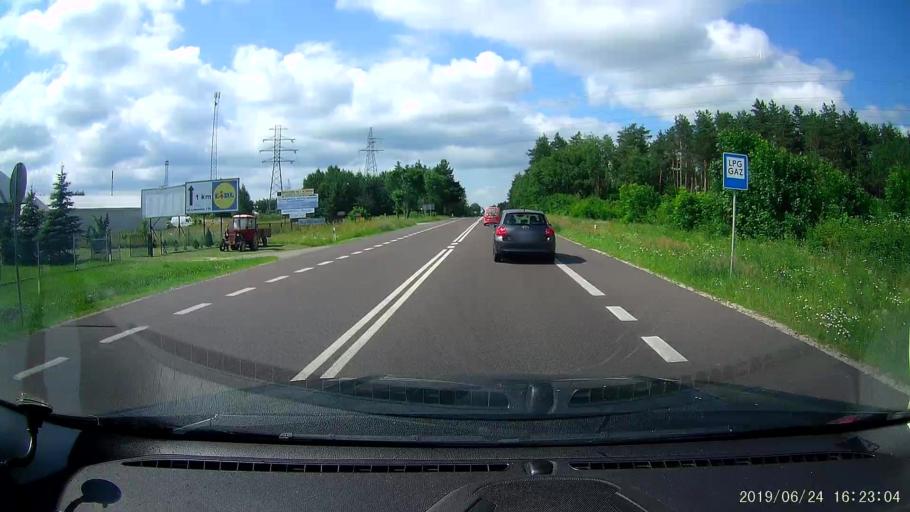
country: PL
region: Lublin Voivodeship
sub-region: Powiat tomaszowski
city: Tomaszow Lubelski
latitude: 50.4276
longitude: 23.4231
